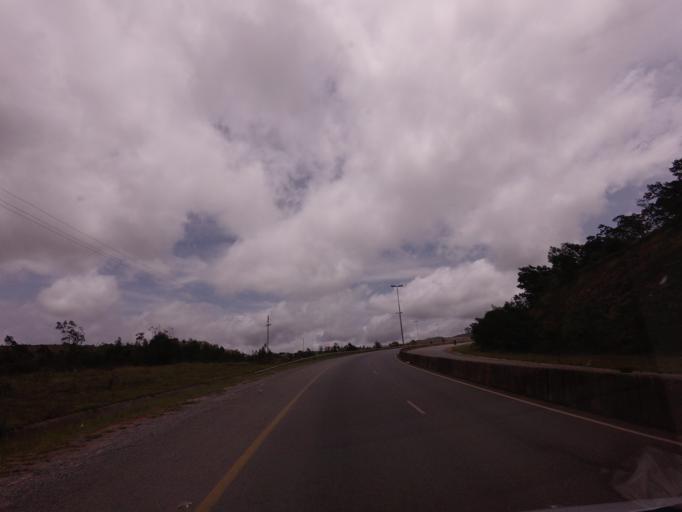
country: SZ
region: Hhohho
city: Mbabane
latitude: -26.2816
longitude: 31.0960
